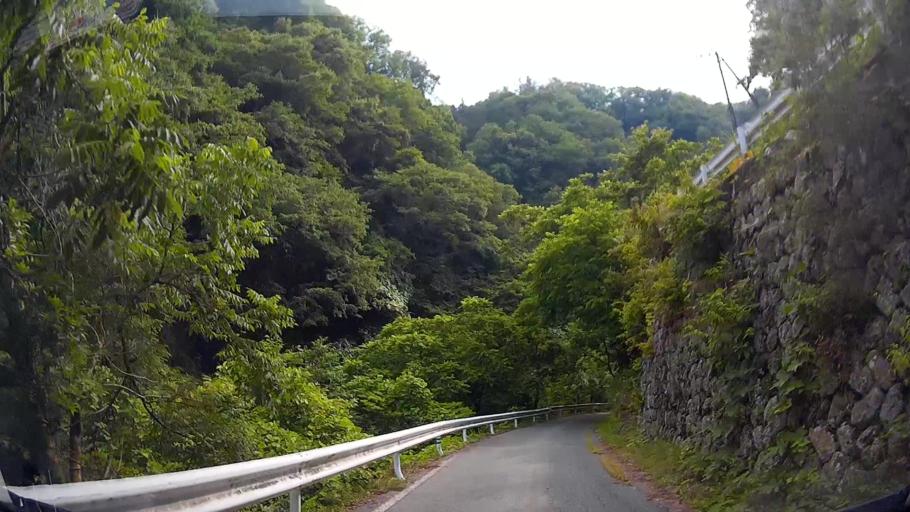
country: JP
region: Nagano
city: Iida
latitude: 35.4890
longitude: 137.8996
